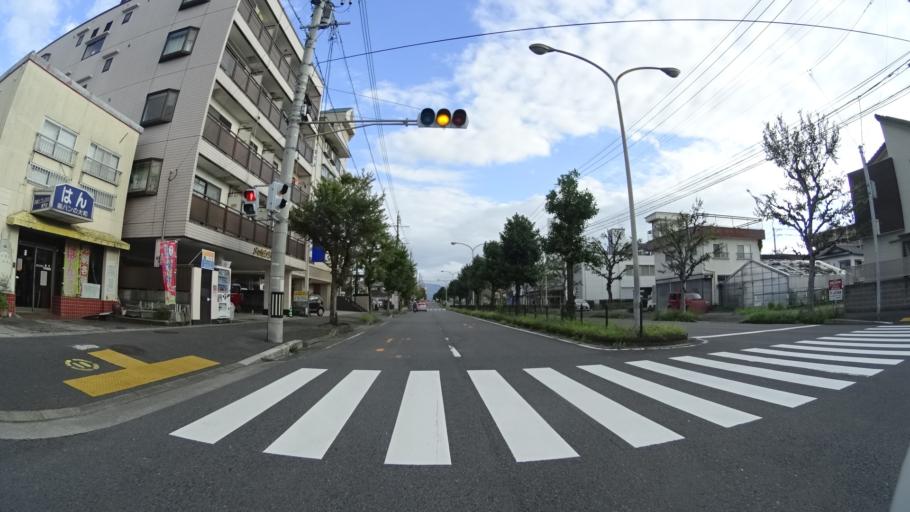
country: JP
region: Oita
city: Beppu
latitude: 33.2941
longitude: 131.4957
